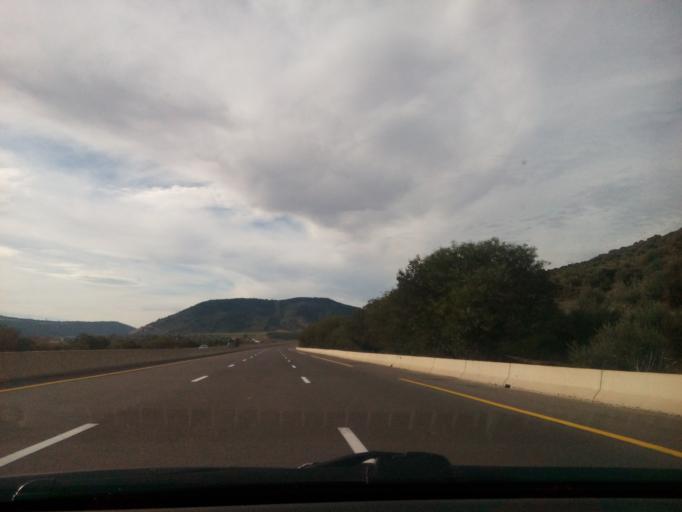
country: DZ
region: Sidi Bel Abbes
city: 'Ain el Berd
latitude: 35.4167
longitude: -0.4787
